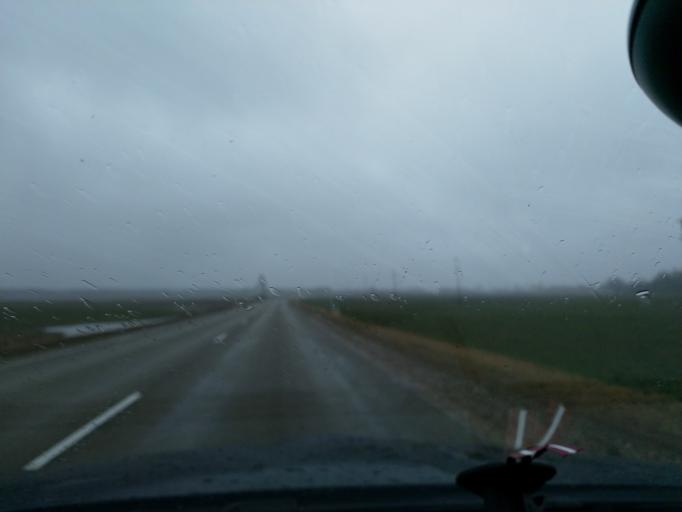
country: LV
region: Saldus Rajons
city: Saldus
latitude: 56.7927
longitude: 22.3185
